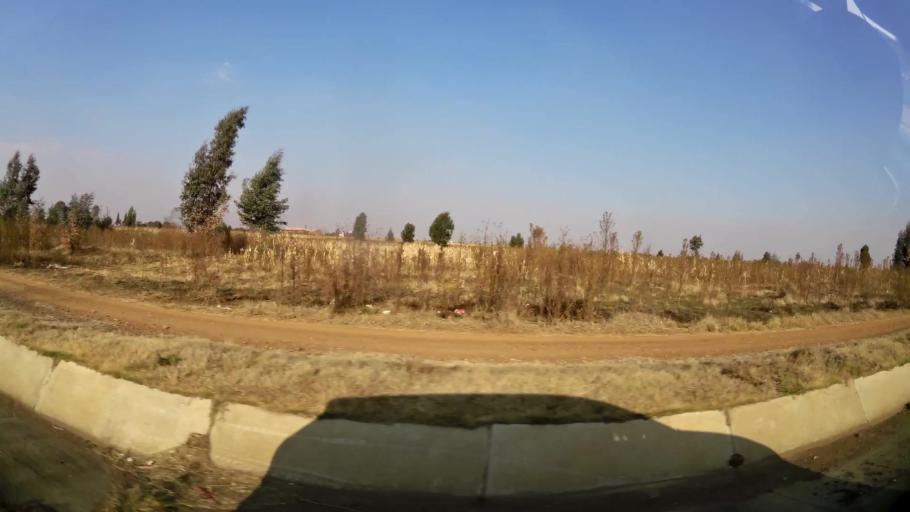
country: ZA
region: Gauteng
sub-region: Ekurhuleni Metropolitan Municipality
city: Benoni
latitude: -26.1406
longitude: 28.3901
